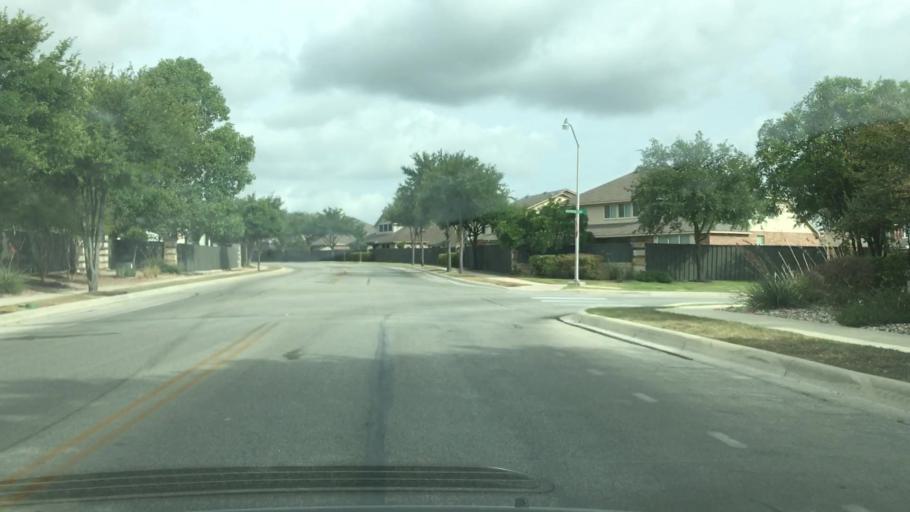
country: US
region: Texas
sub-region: Guadalupe County
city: Cibolo
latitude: 29.5823
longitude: -98.2409
